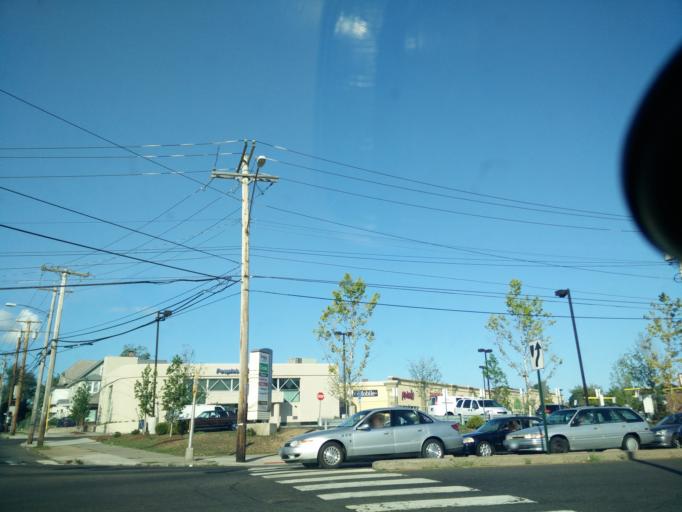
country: US
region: Connecticut
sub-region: Fairfield County
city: Bridgeport
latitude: 41.1830
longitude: -73.2067
